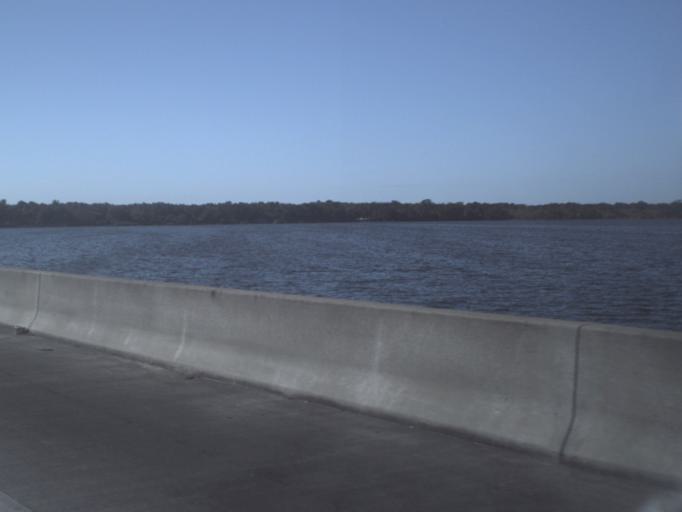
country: US
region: Florida
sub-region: Seminole County
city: Oviedo
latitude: 28.7091
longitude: -81.2377
